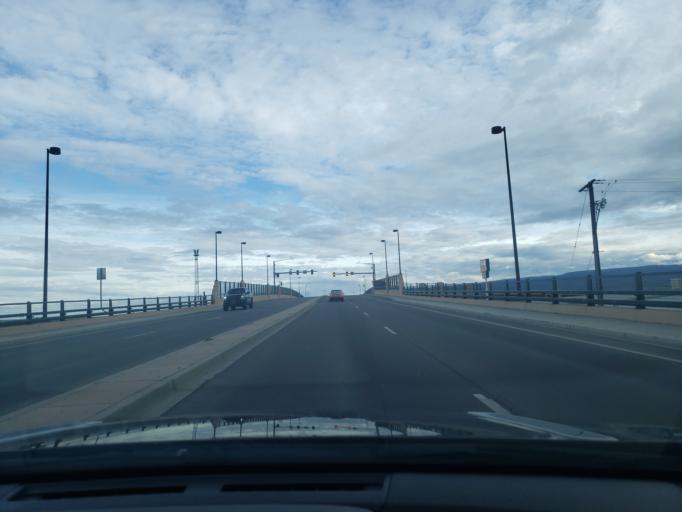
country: US
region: Colorado
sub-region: Mesa County
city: Fruitvale
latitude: 39.0740
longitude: -108.5152
